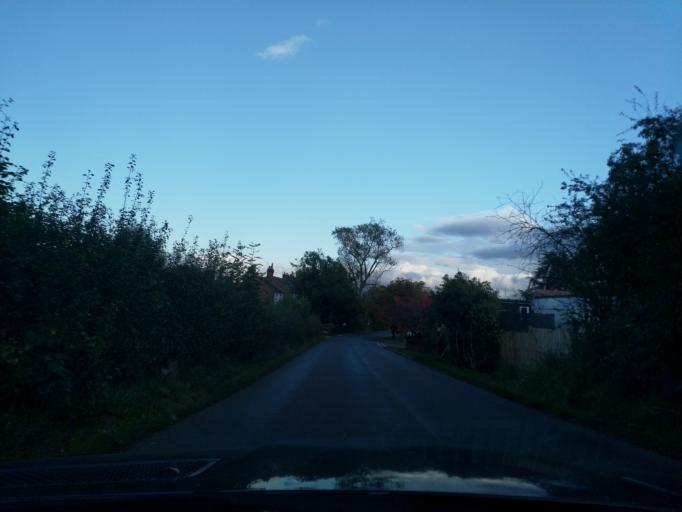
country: GB
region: England
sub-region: Solihull
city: Knowle
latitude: 52.3479
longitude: -1.7233
